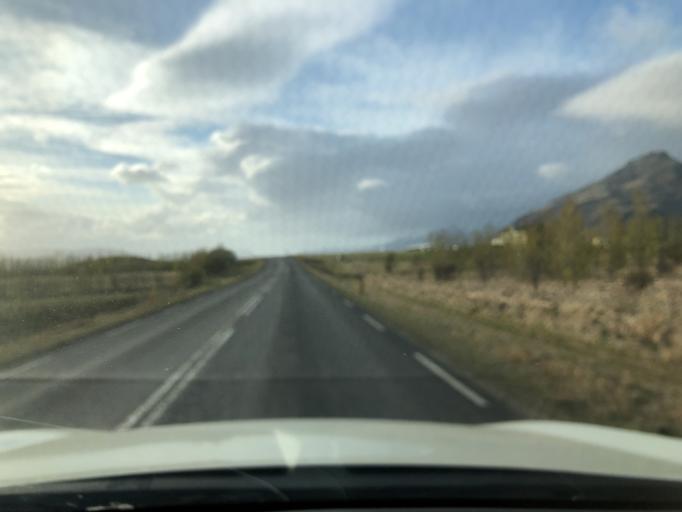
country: IS
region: East
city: Hoefn
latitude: 64.3027
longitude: -15.2051
